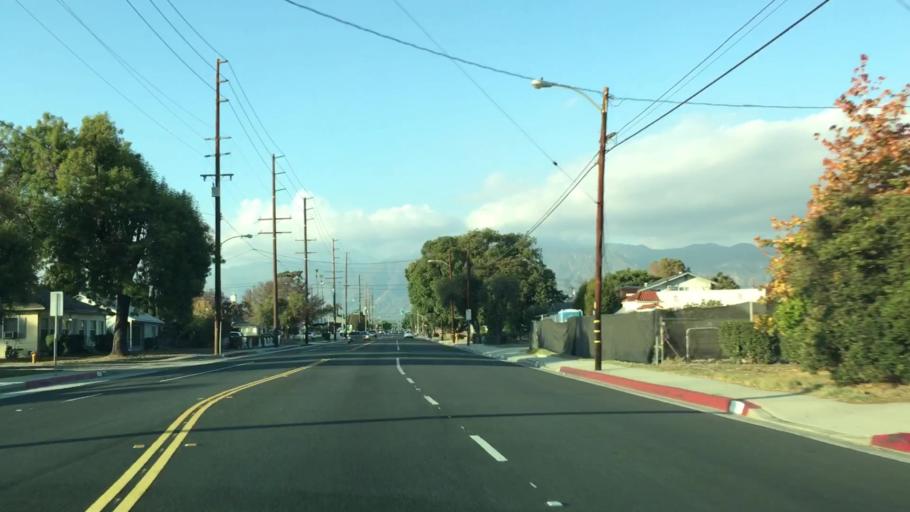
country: US
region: California
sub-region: Los Angeles County
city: Temple City
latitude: 34.0982
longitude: -118.0591
